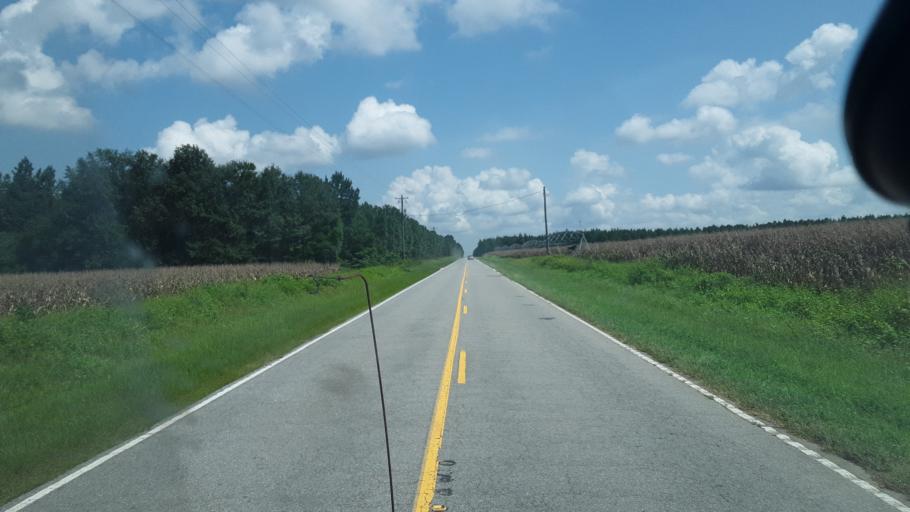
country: US
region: South Carolina
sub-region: Calhoun County
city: Oak Grove
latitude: 33.6532
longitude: -80.9855
